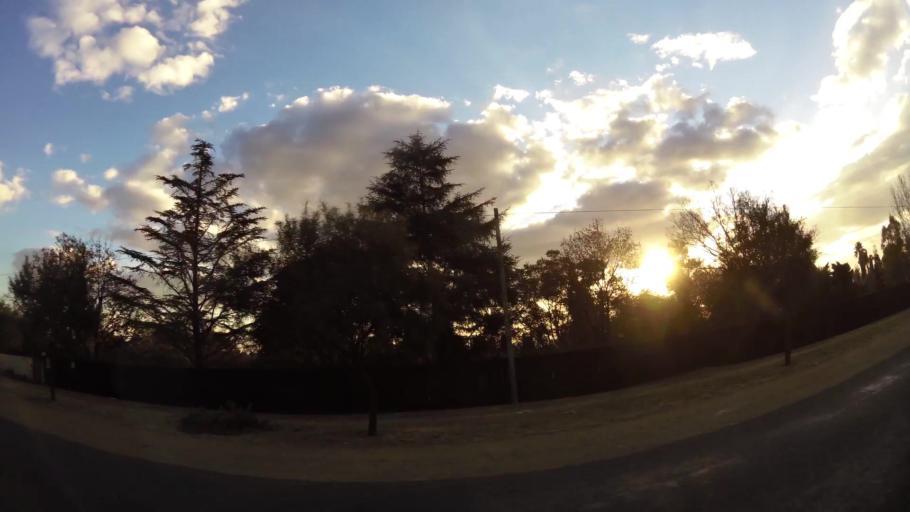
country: ZA
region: Gauteng
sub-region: City of Johannesburg Metropolitan Municipality
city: Midrand
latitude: -25.9778
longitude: 28.1531
